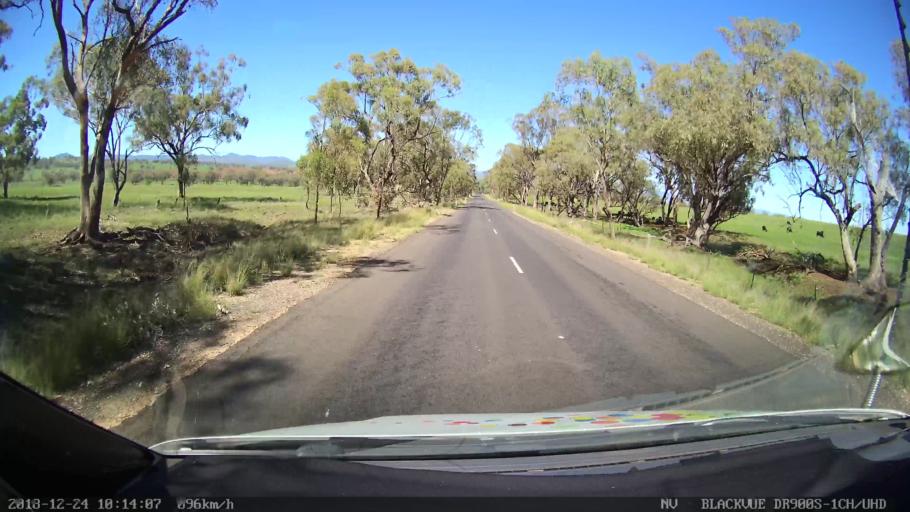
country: AU
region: New South Wales
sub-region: Liverpool Plains
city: Quirindi
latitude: -31.6952
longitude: 150.6326
